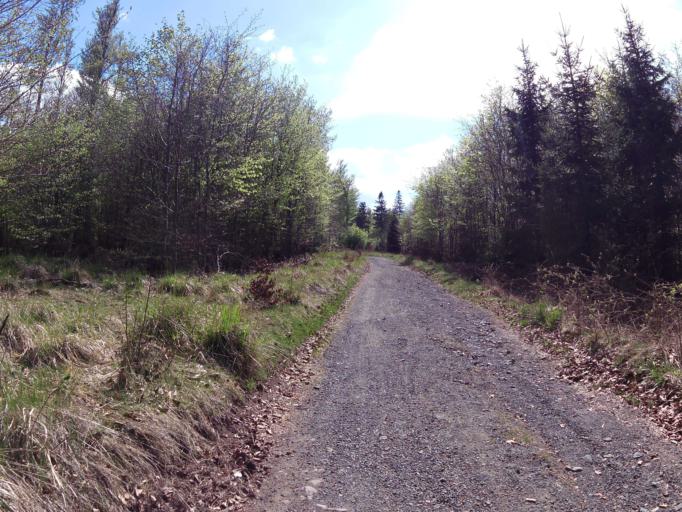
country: DE
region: Thuringia
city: Friedrichroda
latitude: 50.8121
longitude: 10.5417
